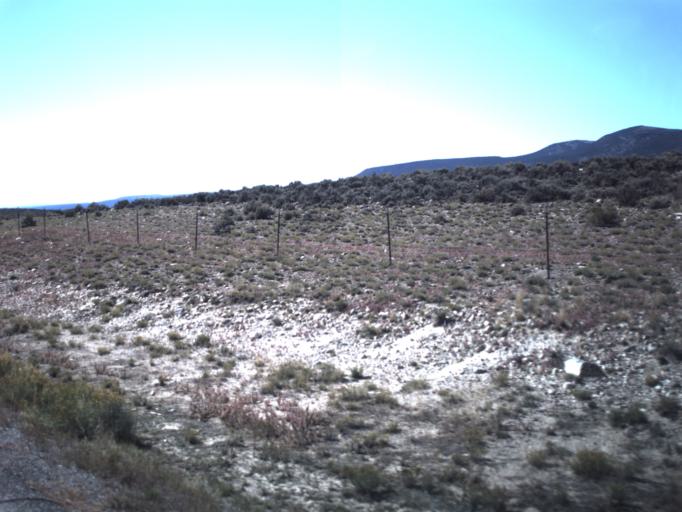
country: US
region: Utah
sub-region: Piute County
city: Junction
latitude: 38.2458
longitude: -111.9876
